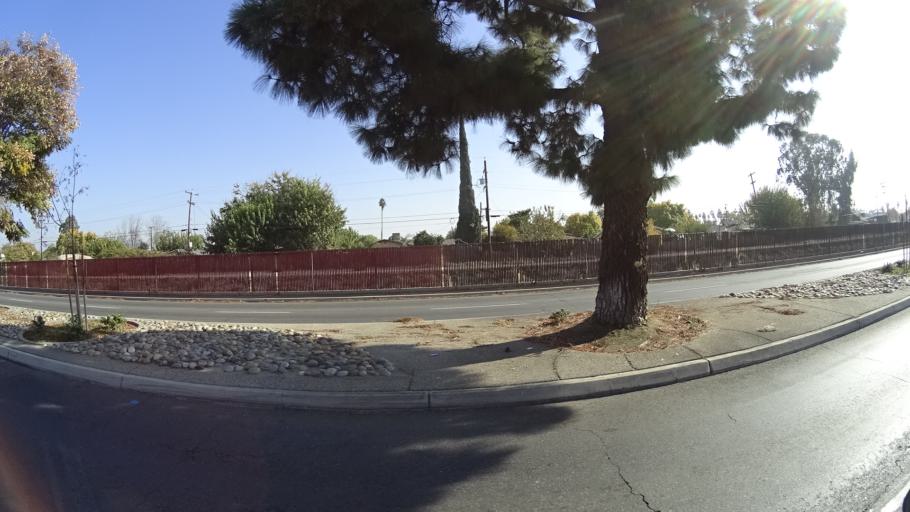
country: US
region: California
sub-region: Kern County
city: Greenfield
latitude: 35.3190
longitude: -119.0213
